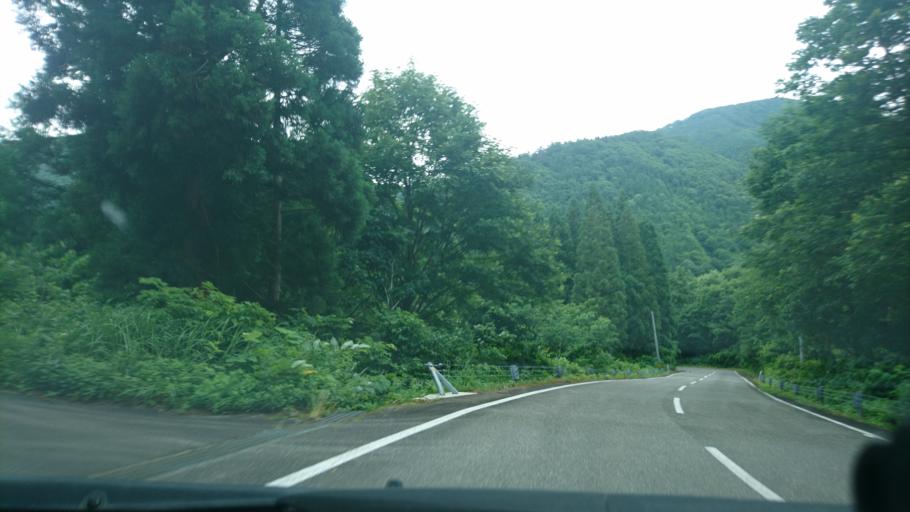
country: JP
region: Akita
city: Yuzawa
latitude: 39.1625
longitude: 140.7484
